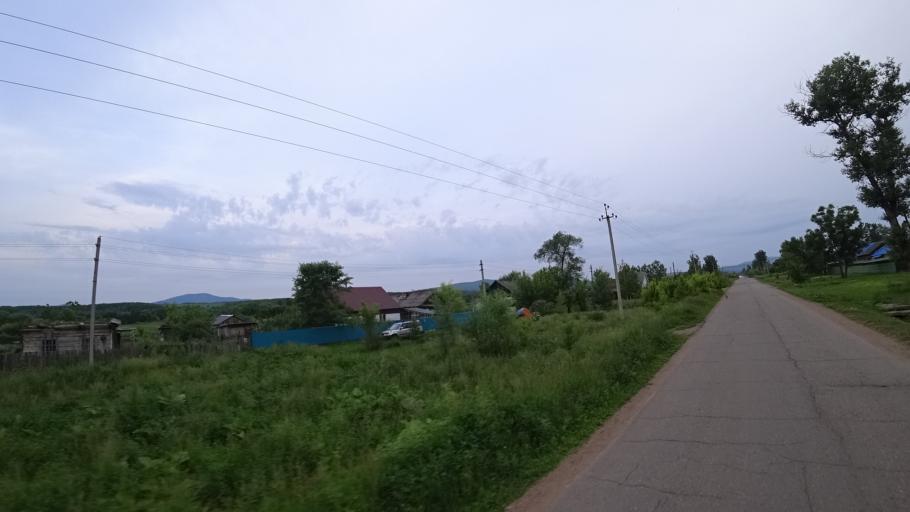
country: RU
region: Primorskiy
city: Novosysoyevka
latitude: 44.2423
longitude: 133.3677
